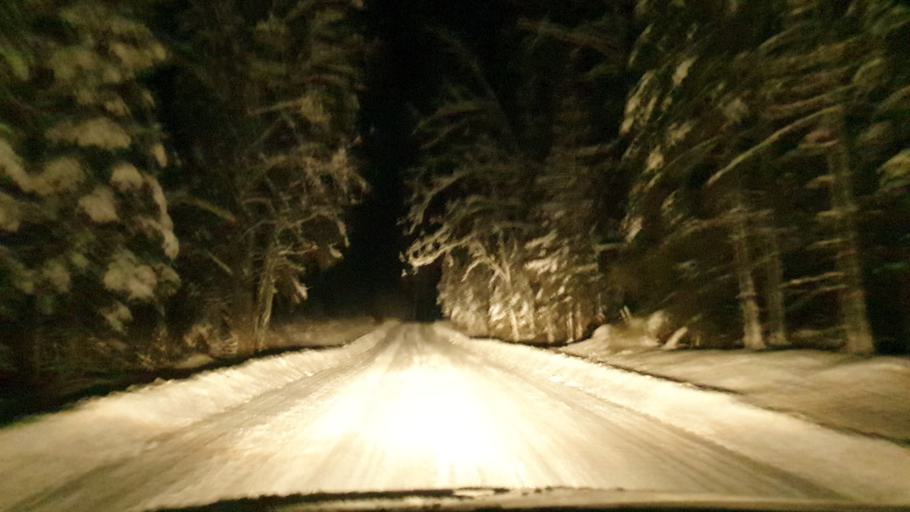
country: EE
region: Vorumaa
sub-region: Antsla vald
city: Vana-Antsla
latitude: 57.9462
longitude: 26.6040
